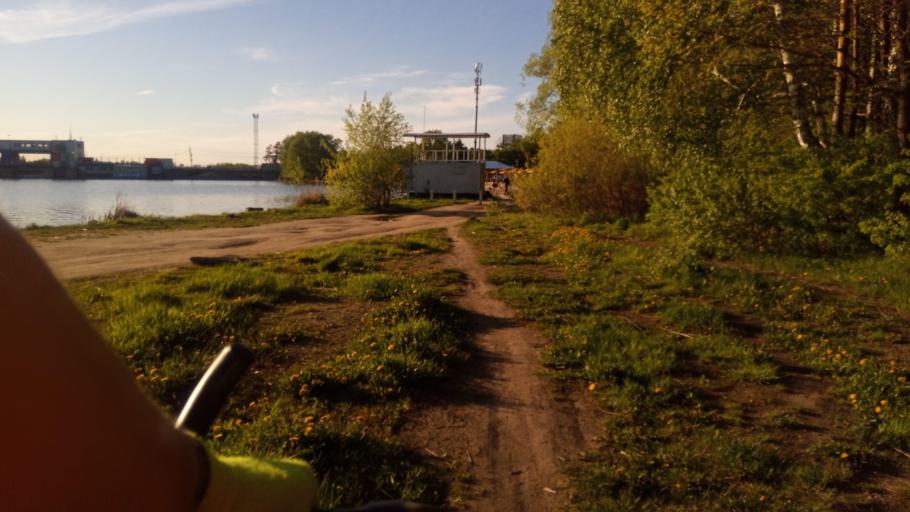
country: RU
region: Chelyabinsk
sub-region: Gorod Chelyabinsk
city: Chelyabinsk
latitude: 55.1443
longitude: 61.3295
